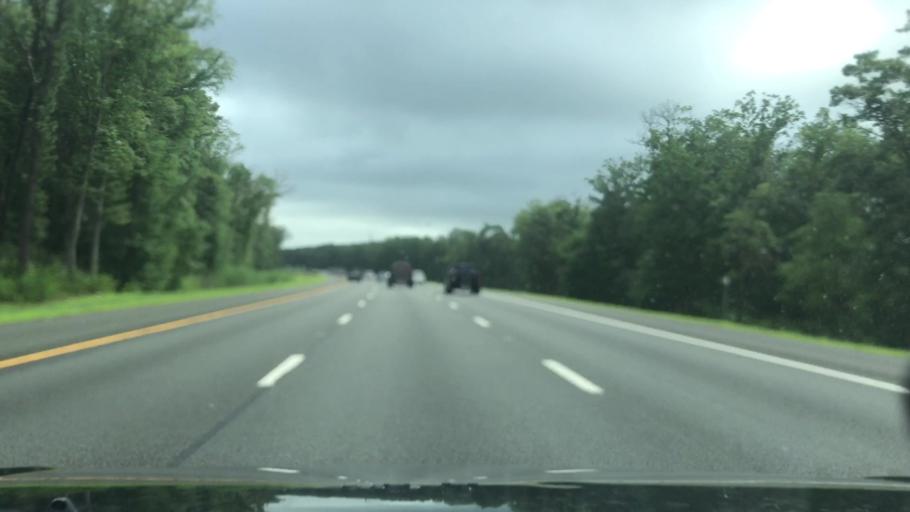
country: US
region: New Jersey
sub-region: Ocean County
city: Leisure Village
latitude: 40.0356
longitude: -74.1817
